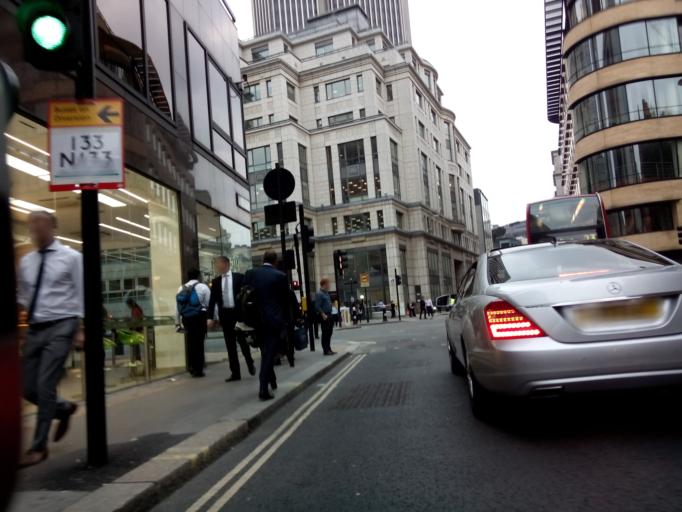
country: GB
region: England
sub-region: Greater London
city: City of London
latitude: 51.5160
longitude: -0.0854
